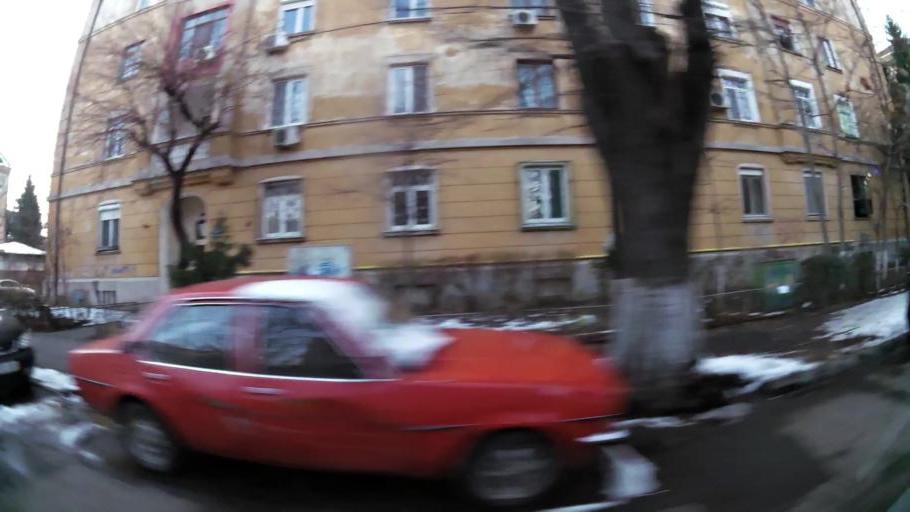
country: RO
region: Ilfov
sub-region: Comuna Fundeni-Dobroesti
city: Fundeni
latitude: 44.4379
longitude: 26.1416
